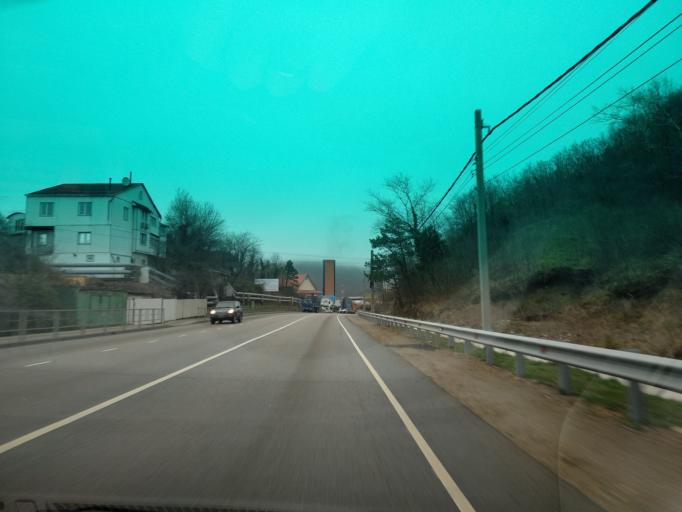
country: RU
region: Krasnodarskiy
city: Tuapse
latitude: 44.1112
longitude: 39.0720
